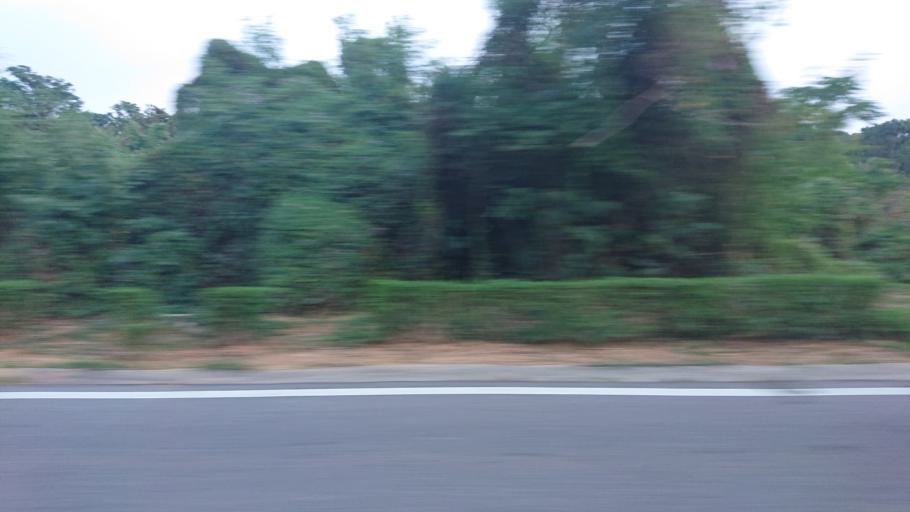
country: TW
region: Fukien
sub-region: Kinmen
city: Jincheng
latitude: 24.4567
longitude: 118.3204
